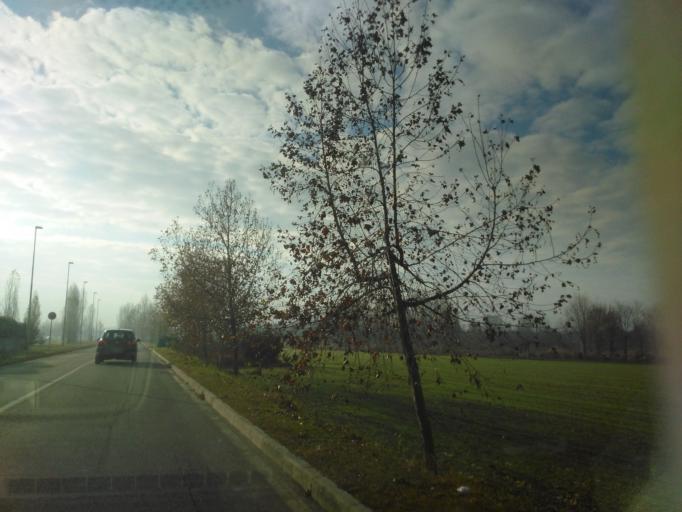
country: IT
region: Lombardy
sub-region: Provincia di Brescia
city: Azzano Mella
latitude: 45.4602
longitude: 10.1240
